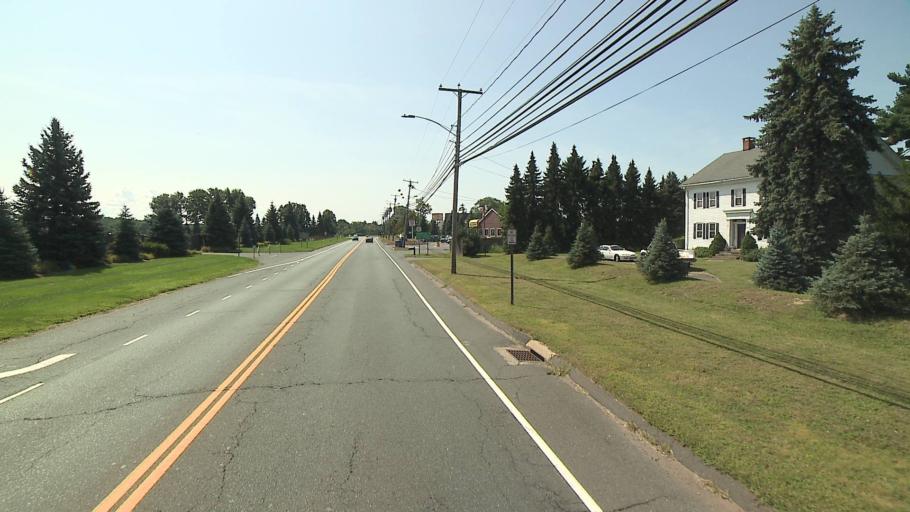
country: US
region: Connecticut
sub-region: Hartford County
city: Windsor Locks
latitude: 41.8922
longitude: -72.6081
